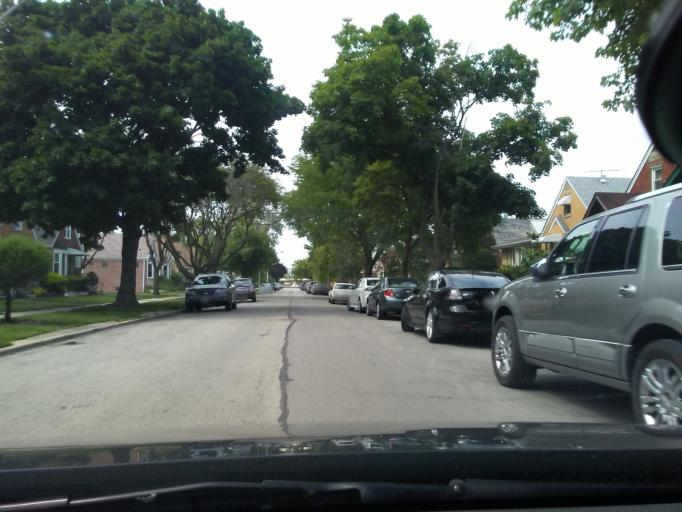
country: US
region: Illinois
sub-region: Cook County
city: Harwood Heights
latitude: 41.9796
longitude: -87.7836
